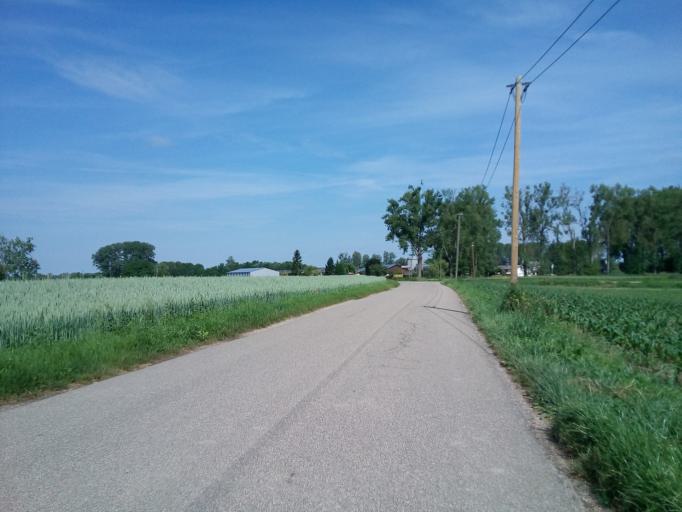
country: FR
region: Alsace
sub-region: Departement du Bas-Rhin
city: Kilstett
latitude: 48.6283
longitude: 7.8855
